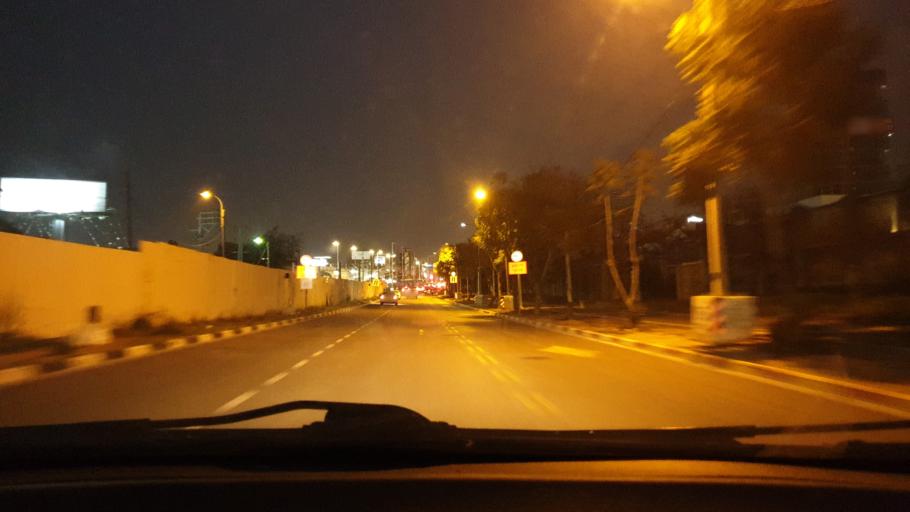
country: IL
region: Tel Aviv
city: Giv`at Shemu'el
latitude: 32.0925
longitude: 34.8508
